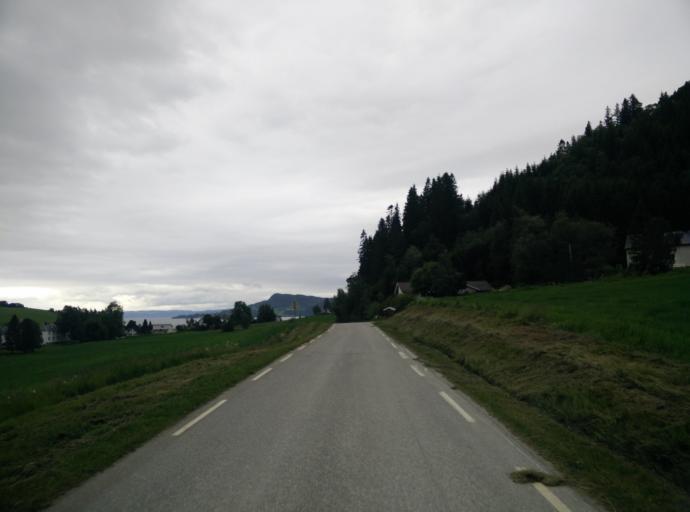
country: NO
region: Sor-Trondelag
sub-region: Skaun
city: Borsa
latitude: 63.3181
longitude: 10.0768
